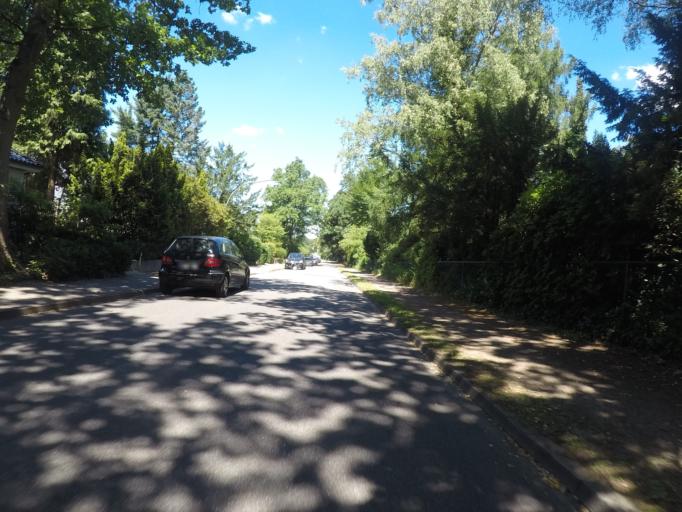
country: DE
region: Schleswig-Holstein
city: Rellingen
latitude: 53.5754
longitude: 9.7991
